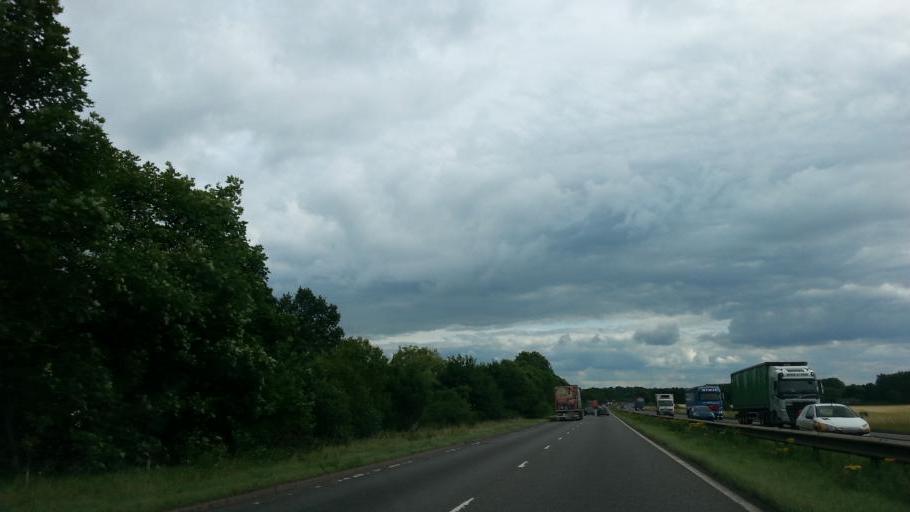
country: GB
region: England
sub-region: Nottinghamshire
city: Babworth
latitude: 53.3331
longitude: -1.0280
